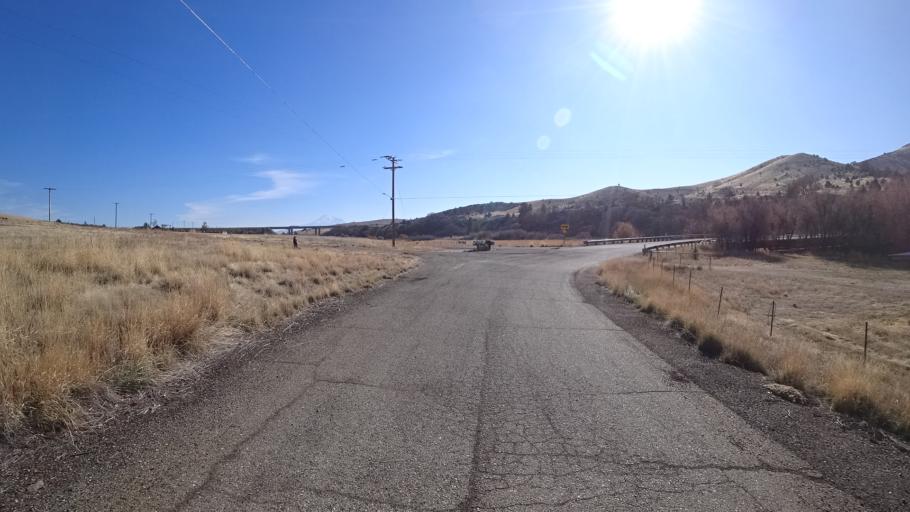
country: US
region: California
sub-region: Siskiyou County
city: Yreka
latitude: 41.7728
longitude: -122.5924
